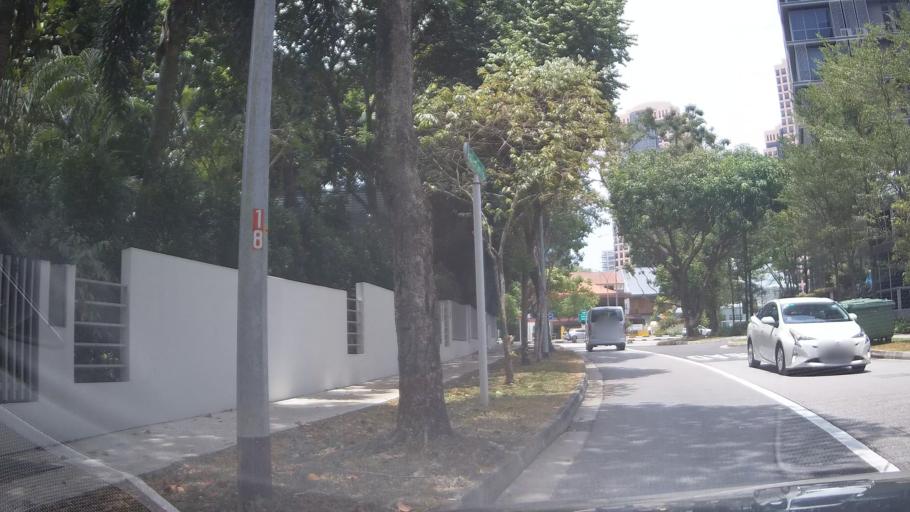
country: SG
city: Singapore
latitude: 1.3008
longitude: 103.8300
